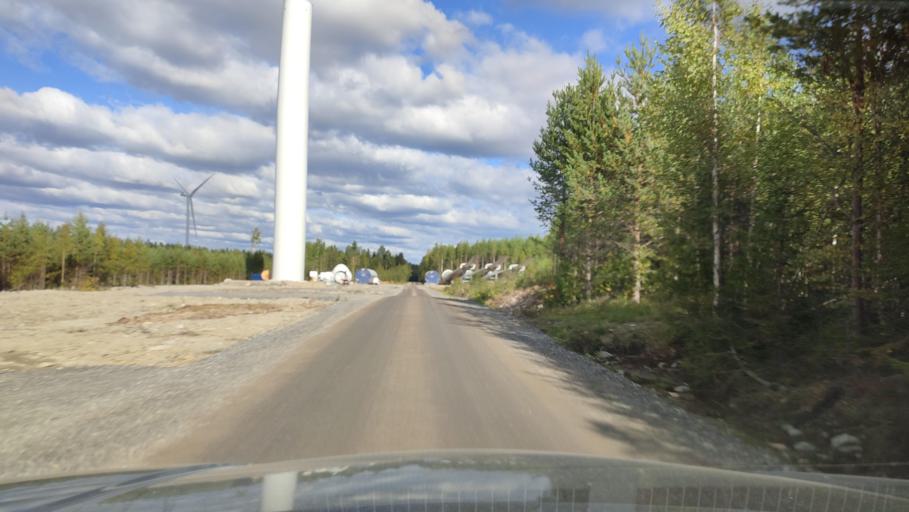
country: FI
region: Southern Ostrobothnia
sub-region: Suupohja
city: Karijoki
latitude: 62.2074
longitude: 21.5996
